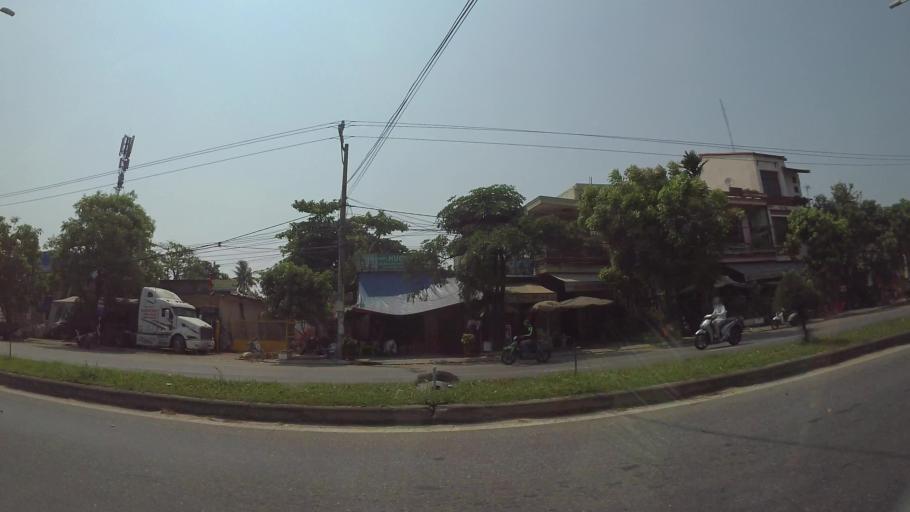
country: VN
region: Da Nang
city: Cam Le
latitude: 15.9770
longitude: 108.2084
